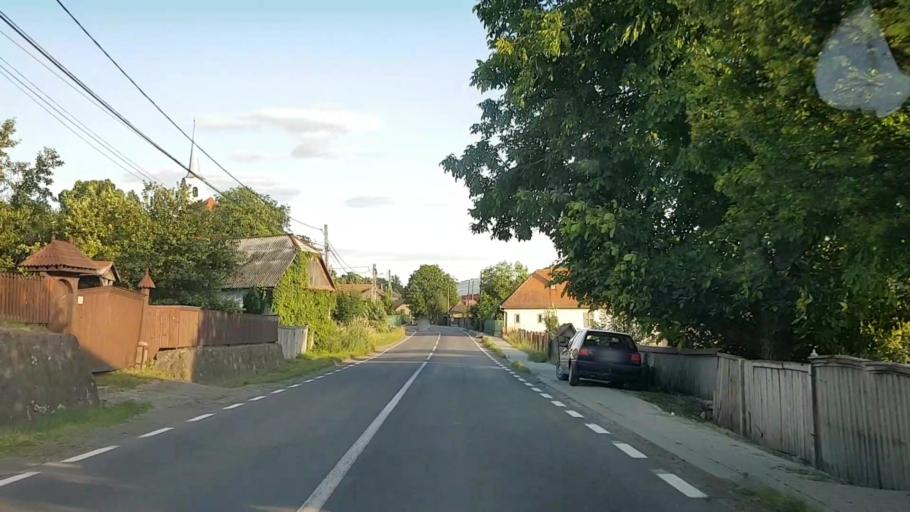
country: RO
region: Harghita
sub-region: Comuna Praid
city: Ocna de Sus
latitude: 46.5273
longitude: 25.1466
